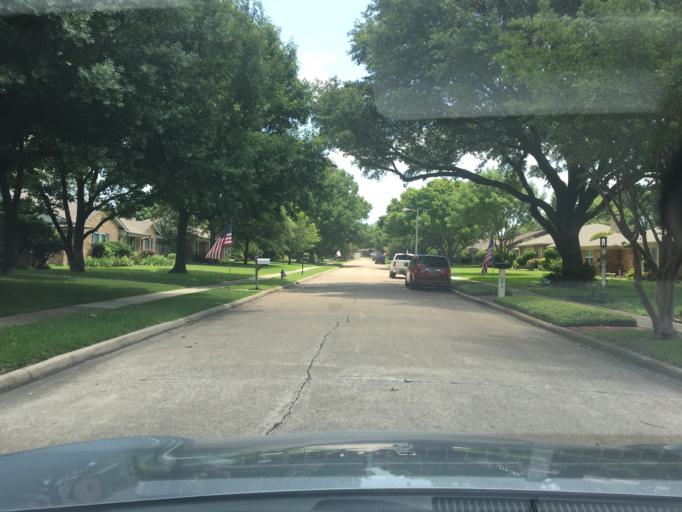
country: US
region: Texas
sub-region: Dallas County
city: Richardson
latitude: 32.9592
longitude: -96.6896
